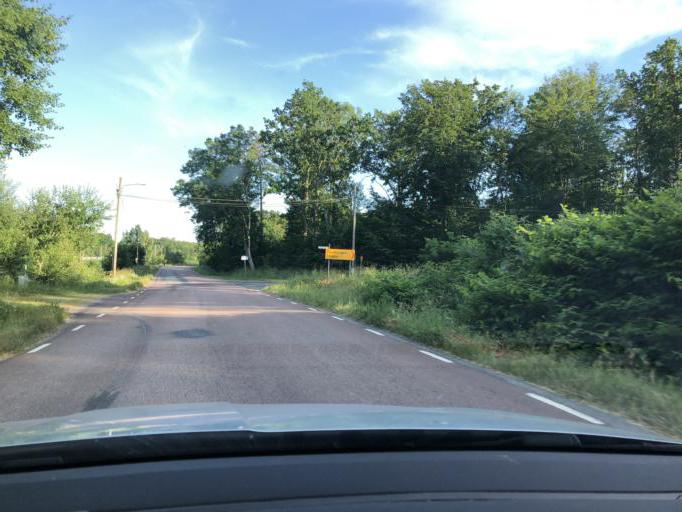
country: SE
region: Blekinge
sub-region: Solvesborgs Kommun
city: Soelvesborg
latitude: 56.1429
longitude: 14.6056
